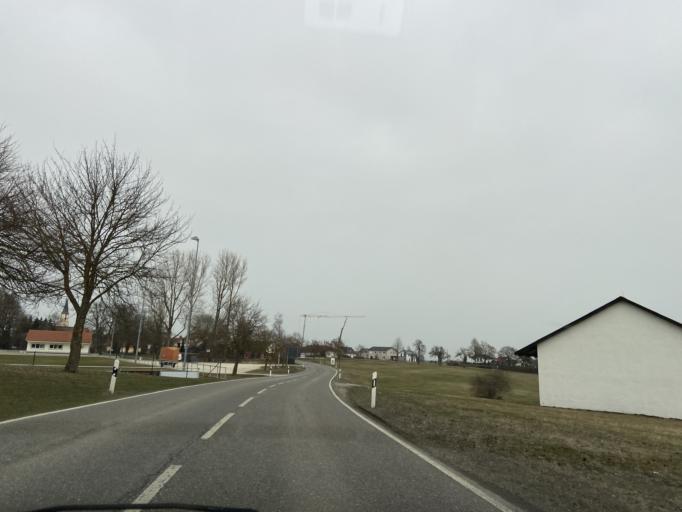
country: DE
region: Baden-Wuerttemberg
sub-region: Tuebingen Region
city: Hettingen
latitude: 48.1848
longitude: 9.2748
